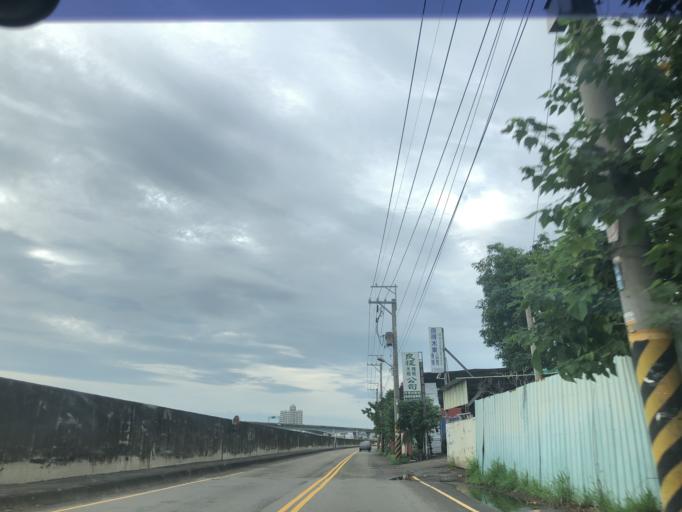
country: TW
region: Taiwan
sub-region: Taichung City
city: Taichung
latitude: 24.1178
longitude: 120.7027
